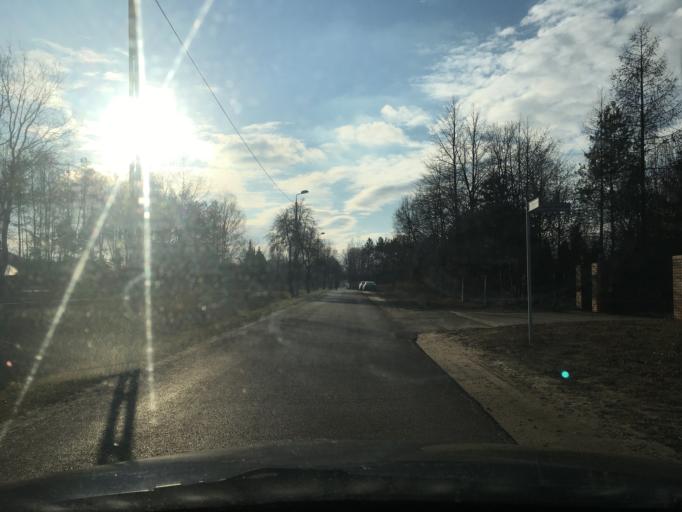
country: PL
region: Masovian Voivodeship
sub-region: Powiat piaseczynski
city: Lesznowola
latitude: 52.0304
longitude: 20.9520
